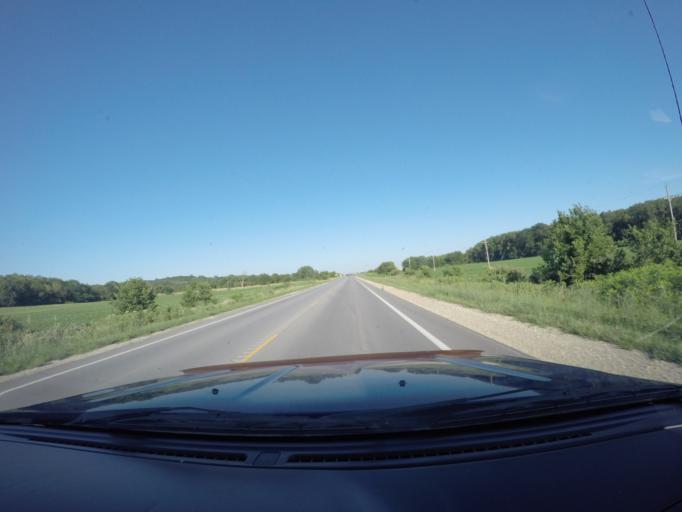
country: US
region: Kansas
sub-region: Douglas County
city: Lawrence
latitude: 39.0674
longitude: -95.3391
